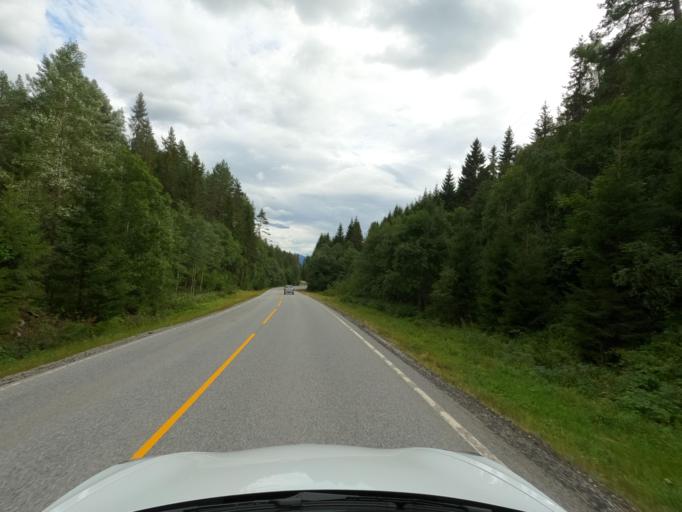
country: NO
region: Telemark
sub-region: Hjartdal
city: Sauland
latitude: 59.8235
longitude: 8.9816
